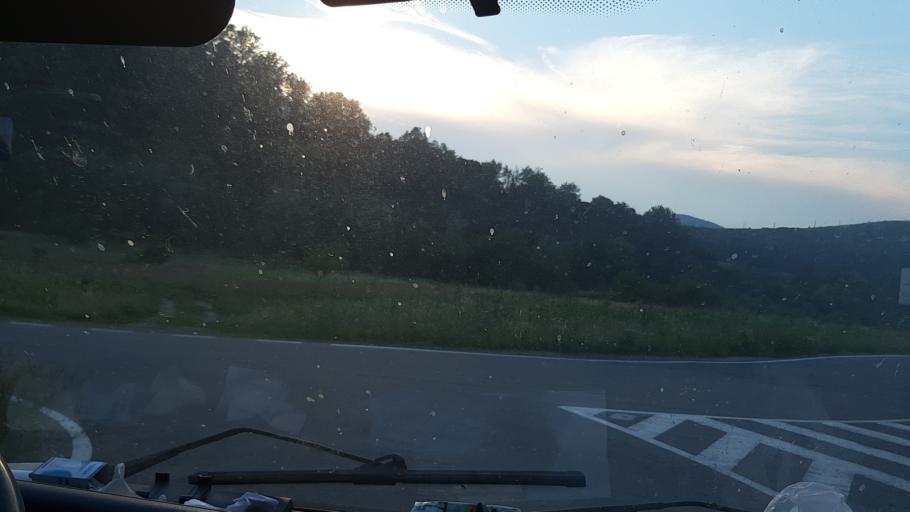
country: RO
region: Caras-Severin
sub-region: Municipiul Resita
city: Calnic
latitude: 45.3699
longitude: 21.7990
